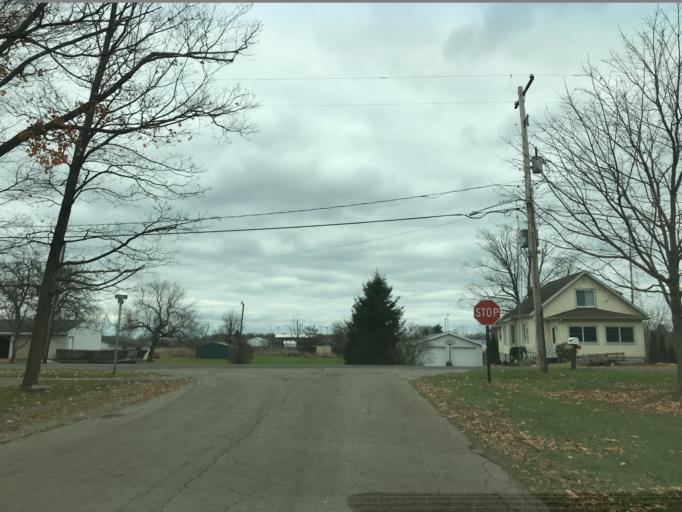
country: US
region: Michigan
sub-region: Eaton County
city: Grand Ledge
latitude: 42.8103
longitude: -84.7890
